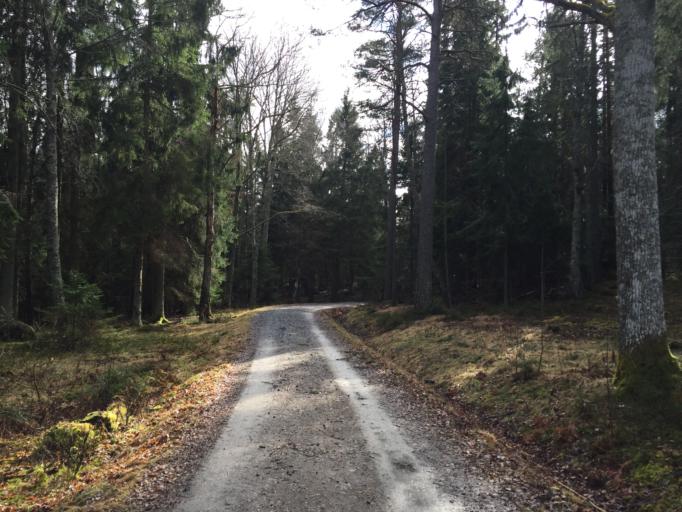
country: SE
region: Stockholm
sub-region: Salems Kommun
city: Ronninge
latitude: 59.2206
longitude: 17.7375
